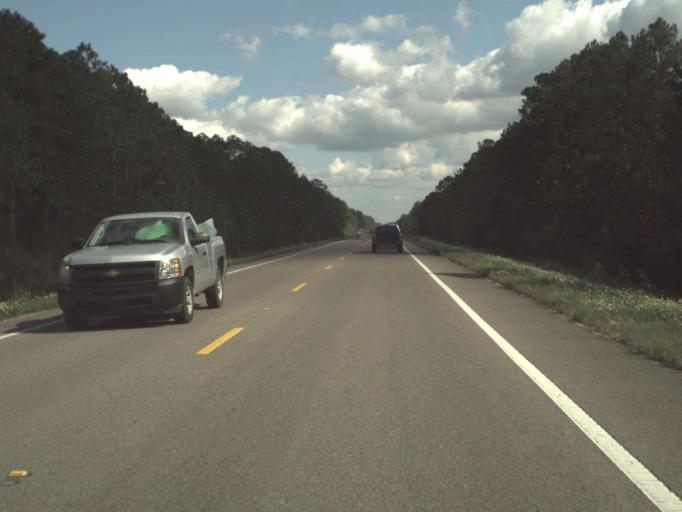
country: US
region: Florida
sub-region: Walton County
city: Freeport
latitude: 30.4608
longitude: -85.9277
